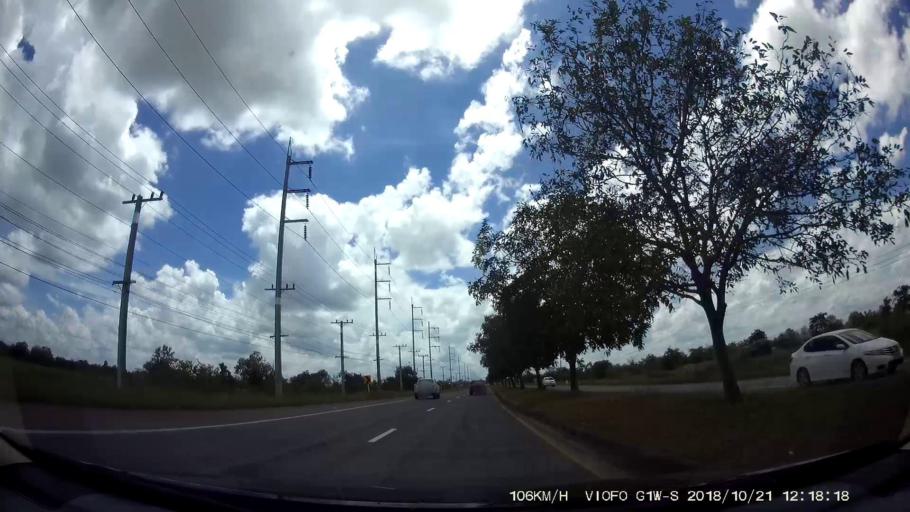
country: TH
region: Nakhon Ratchasima
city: Dan Khun Thot
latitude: 15.3186
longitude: 101.8180
